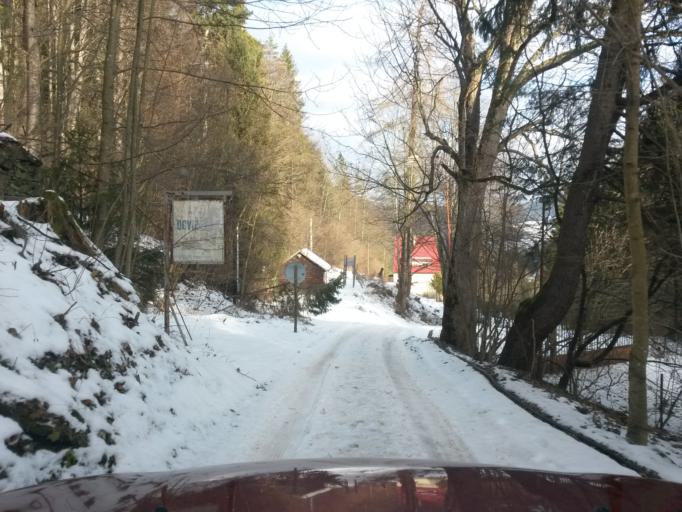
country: SK
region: Kosicky
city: Spisska Nova Ves
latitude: 48.8437
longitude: 20.5855
